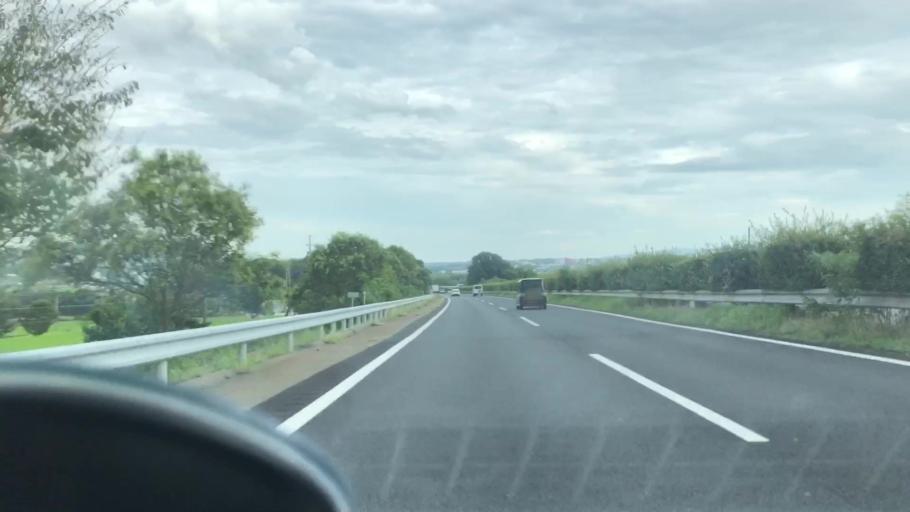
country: JP
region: Hyogo
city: Yashiro
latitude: 34.9300
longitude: 134.9384
